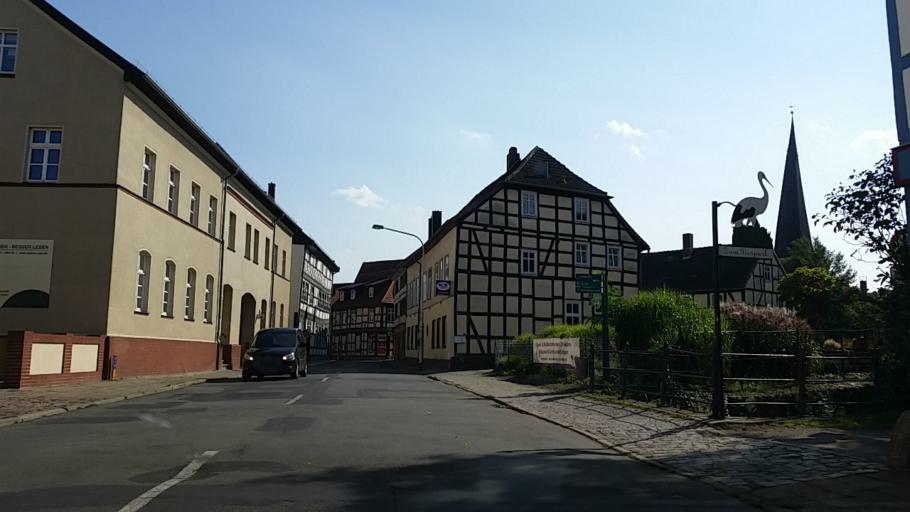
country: DE
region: Saxony-Anhalt
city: Salzwedel
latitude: 52.8517
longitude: 11.1491
